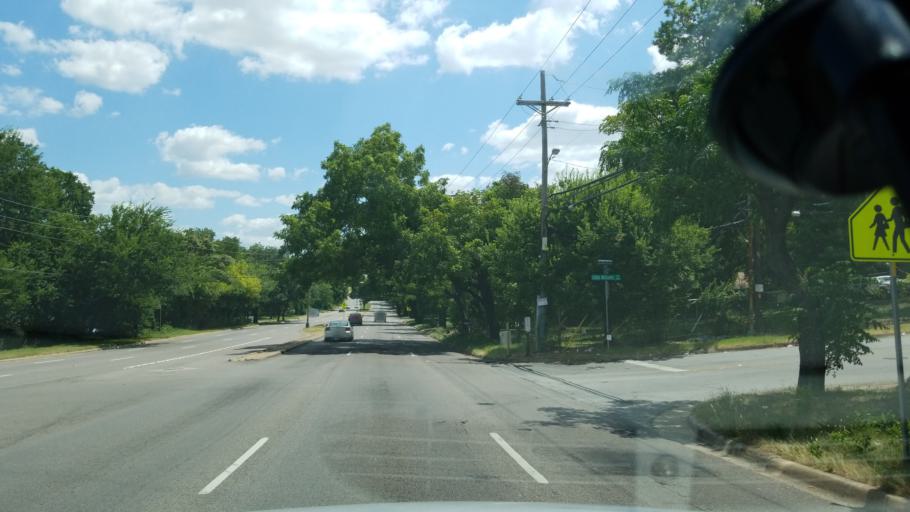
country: US
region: Texas
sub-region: Dallas County
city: Cockrell Hill
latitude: 32.6984
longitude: -96.8572
